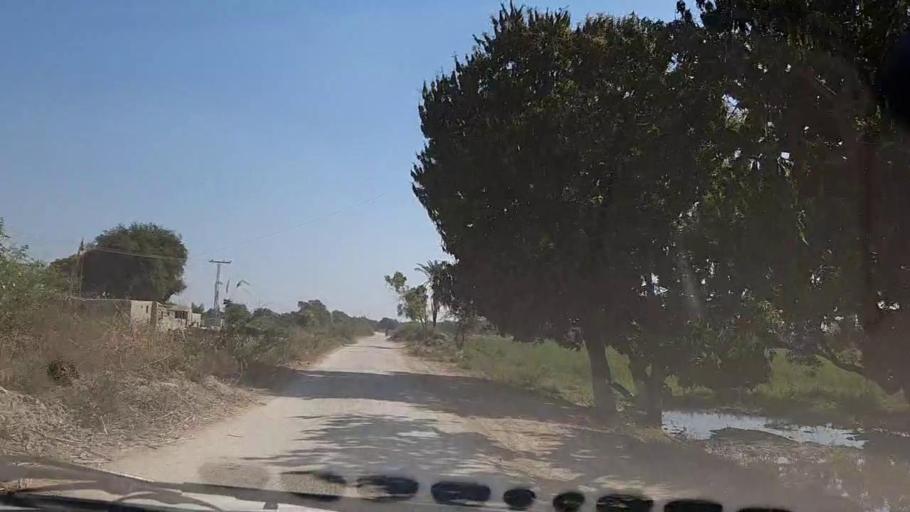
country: PK
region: Sindh
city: Mirpur Khas
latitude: 25.4712
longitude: 69.0324
